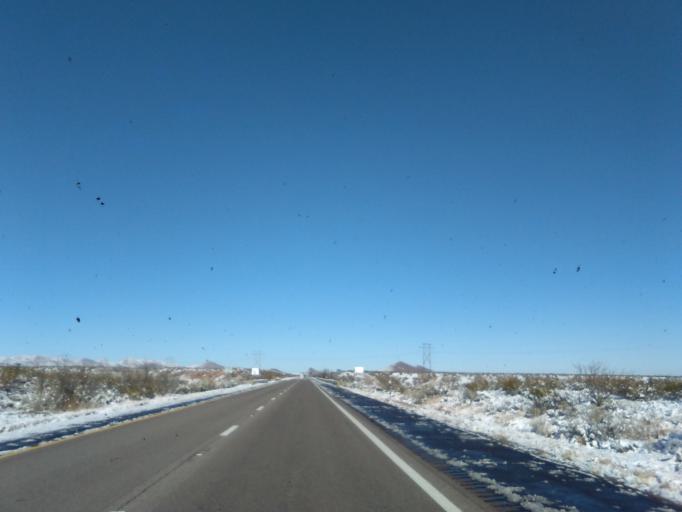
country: US
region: New Mexico
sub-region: Socorro County
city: Socorro
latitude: 33.7140
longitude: -107.0355
